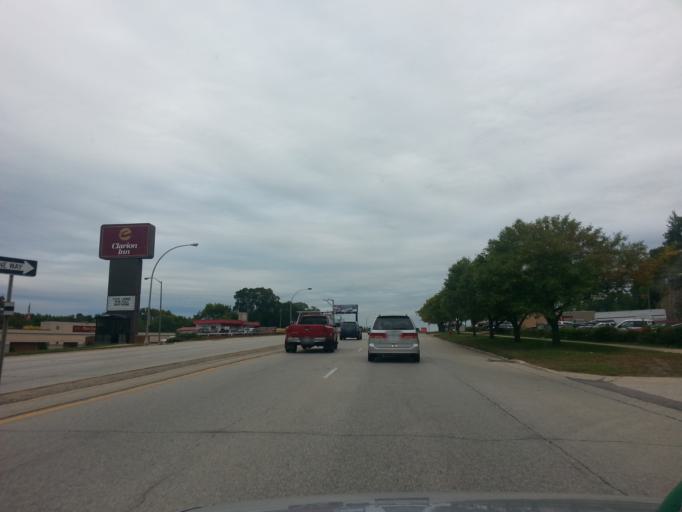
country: US
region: Minnesota
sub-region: Olmsted County
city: Rochester
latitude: 43.9995
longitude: -92.4644
